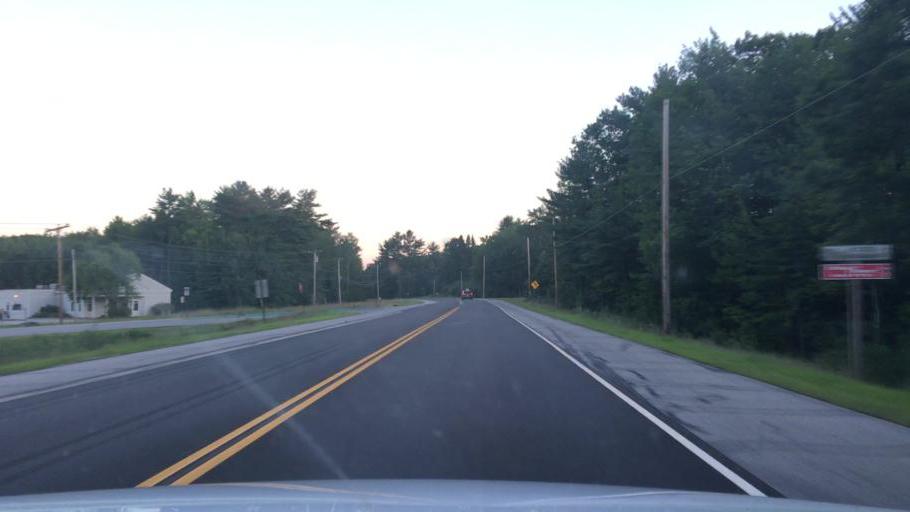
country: US
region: Maine
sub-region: Androscoggin County
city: Turner
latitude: 44.2459
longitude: -70.2602
